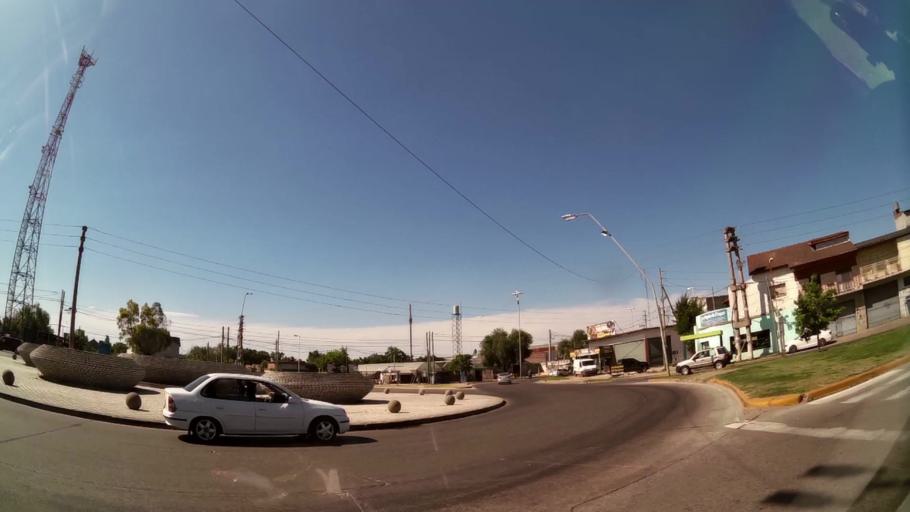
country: AR
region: Buenos Aires
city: Santa Catalina - Dique Lujan
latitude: -34.4910
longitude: -58.6990
